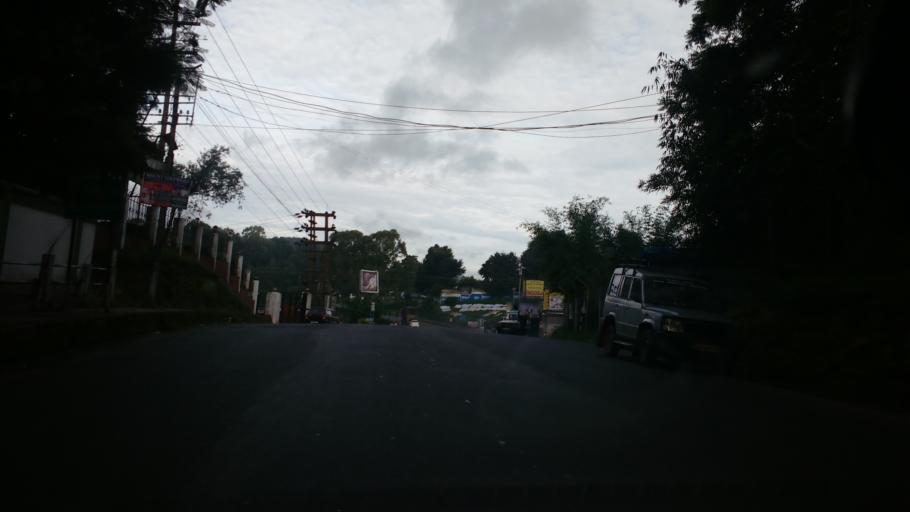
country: IN
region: Meghalaya
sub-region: East Khasi Hills
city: Shillong
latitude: 25.5715
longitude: 91.8720
